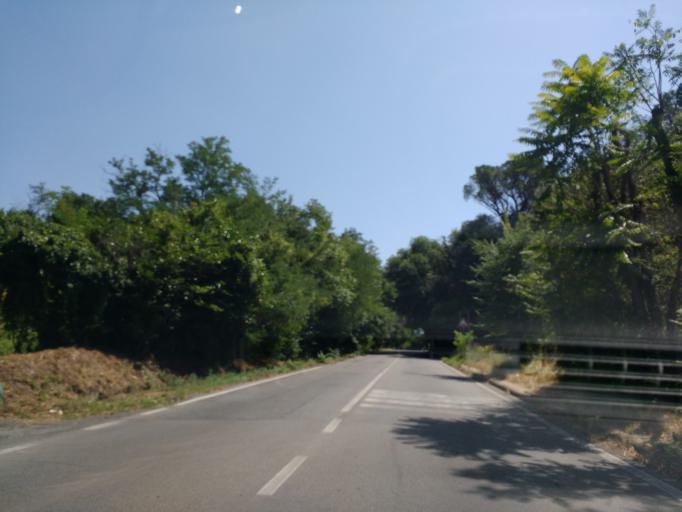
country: IT
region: Latium
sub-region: Citta metropolitana di Roma Capitale
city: Grottaferrata
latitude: 41.7967
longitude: 12.6828
